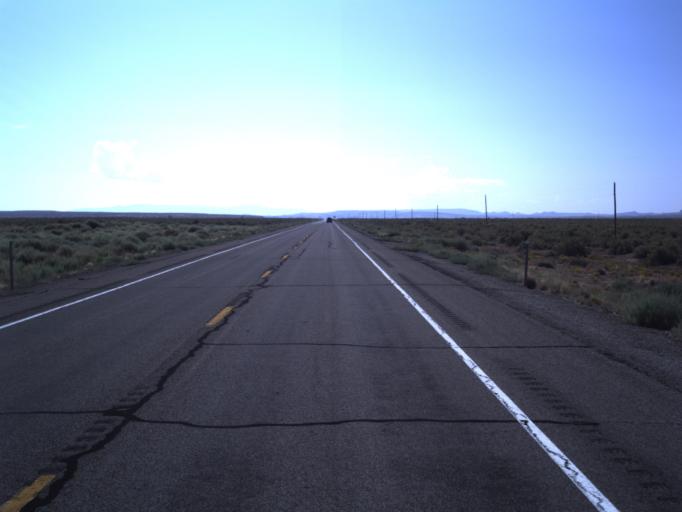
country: US
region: Utah
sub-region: San Juan County
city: Blanding
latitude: 37.1961
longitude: -109.6003
